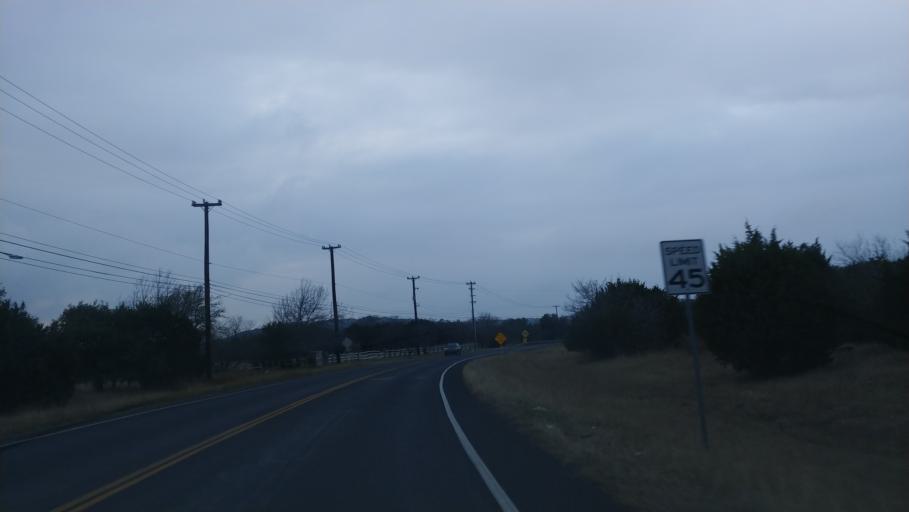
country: US
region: Texas
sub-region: Bexar County
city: Cross Mountain
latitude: 29.6776
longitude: -98.6653
